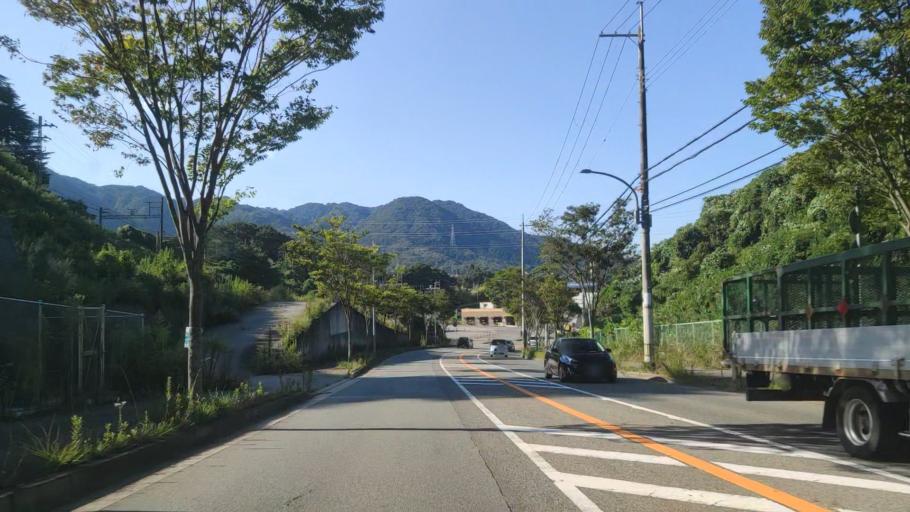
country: JP
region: Hyogo
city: Kobe
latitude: 34.7747
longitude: 135.1940
